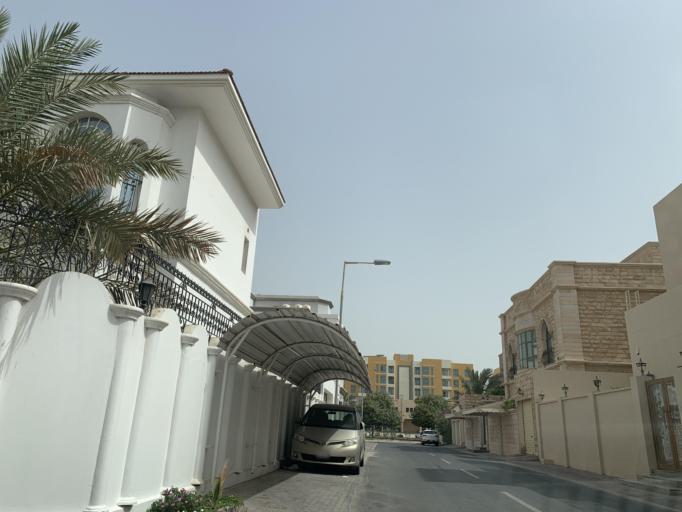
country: BH
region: Northern
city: Madinat `Isa
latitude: 26.1687
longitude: 50.5504
